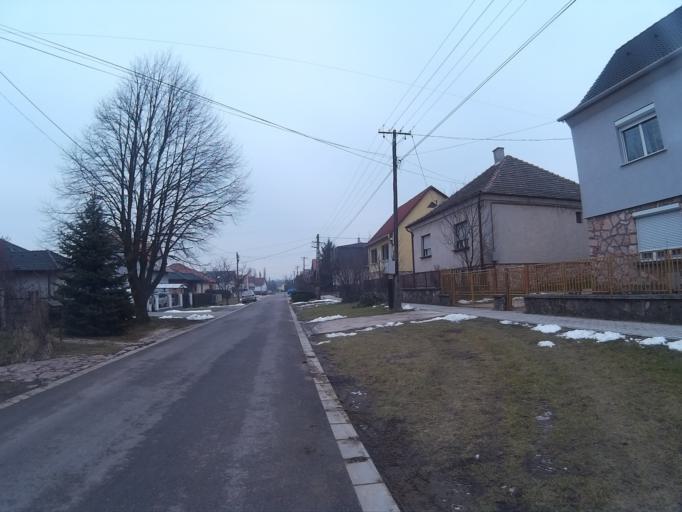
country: HU
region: Komarom-Esztergom
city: Tarjan
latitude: 47.6061
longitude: 18.5140
